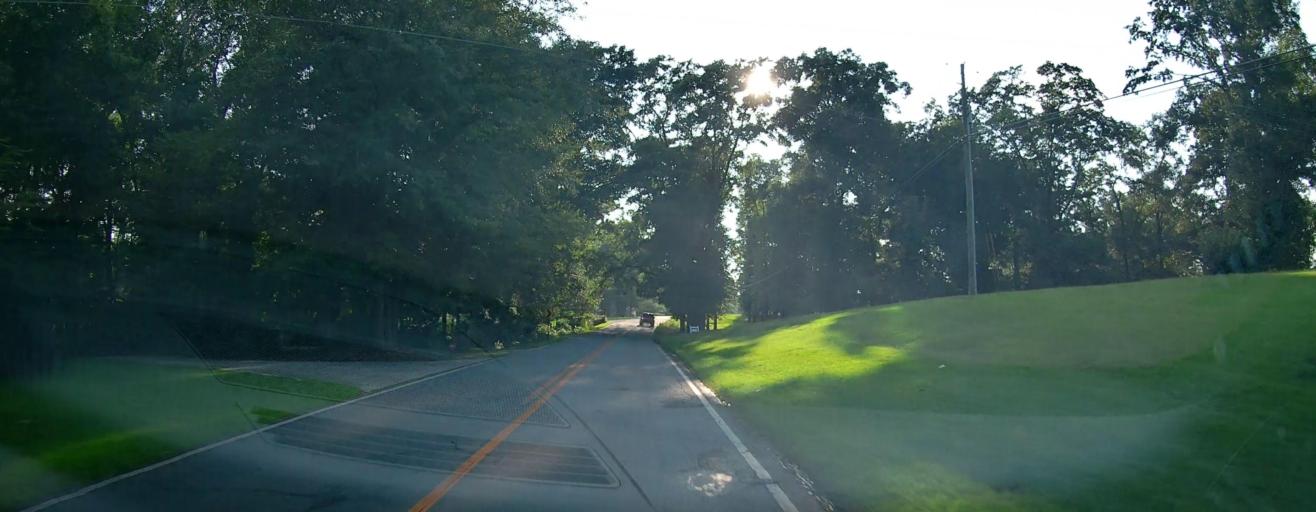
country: US
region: Georgia
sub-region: Peach County
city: Byron
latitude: 32.7169
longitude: -83.7418
